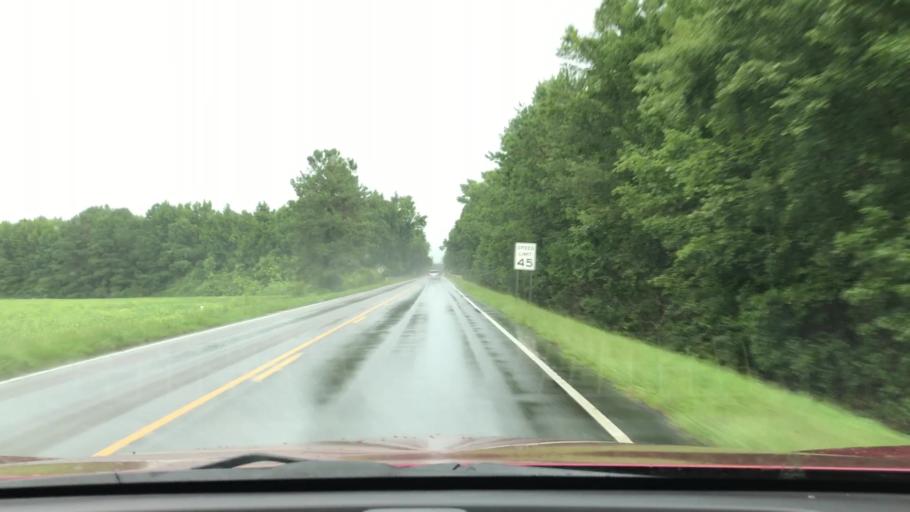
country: US
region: South Carolina
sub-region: Horry County
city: Socastee
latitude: 33.6848
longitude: -79.1233
